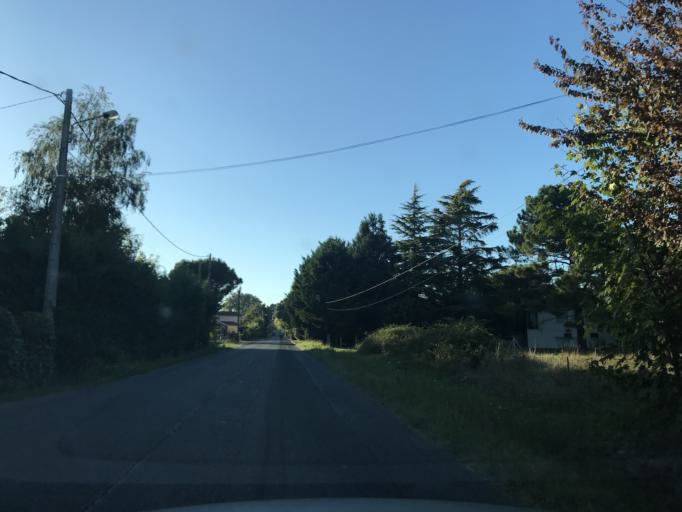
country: FR
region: Aquitaine
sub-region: Departement de la Gironde
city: Mouliets-et-Villemartin
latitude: 44.8472
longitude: -0.0383
